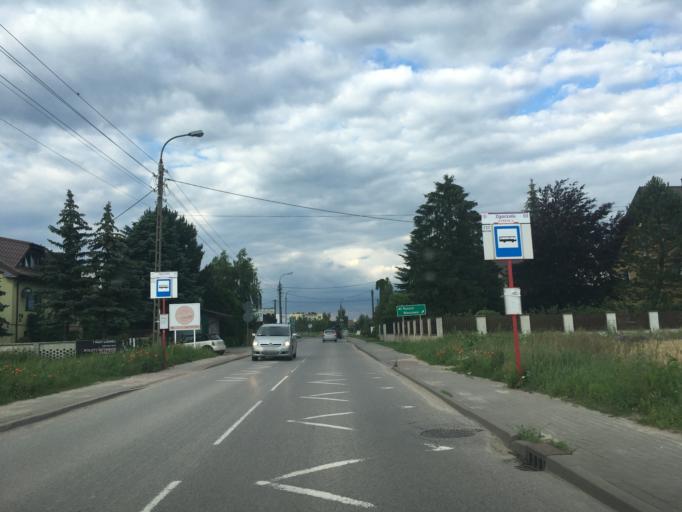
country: PL
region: Masovian Voivodeship
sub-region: Powiat piaseczynski
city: Mysiadlo
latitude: 52.1101
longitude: 20.9835
